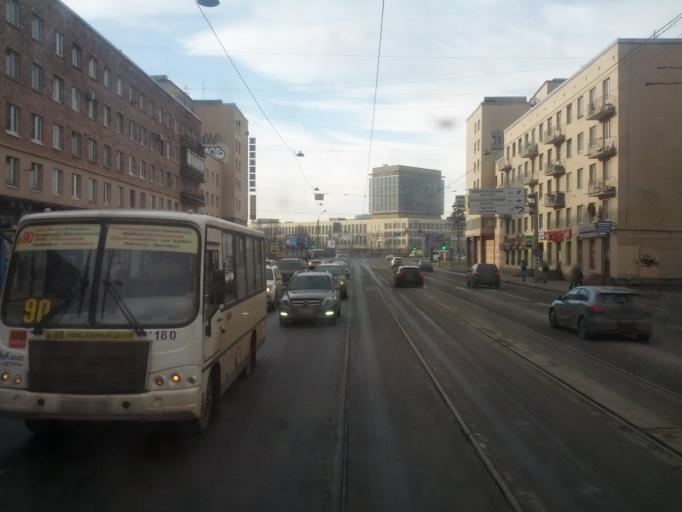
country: RU
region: St.-Petersburg
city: Centralniy
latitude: 59.9445
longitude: 30.4132
